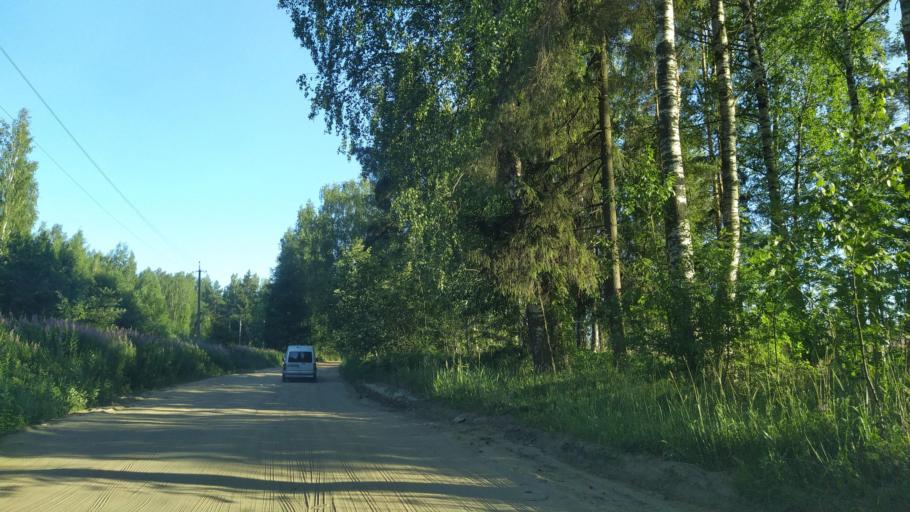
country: RU
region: Leningrad
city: Koltushi
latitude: 59.9093
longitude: 30.7365
